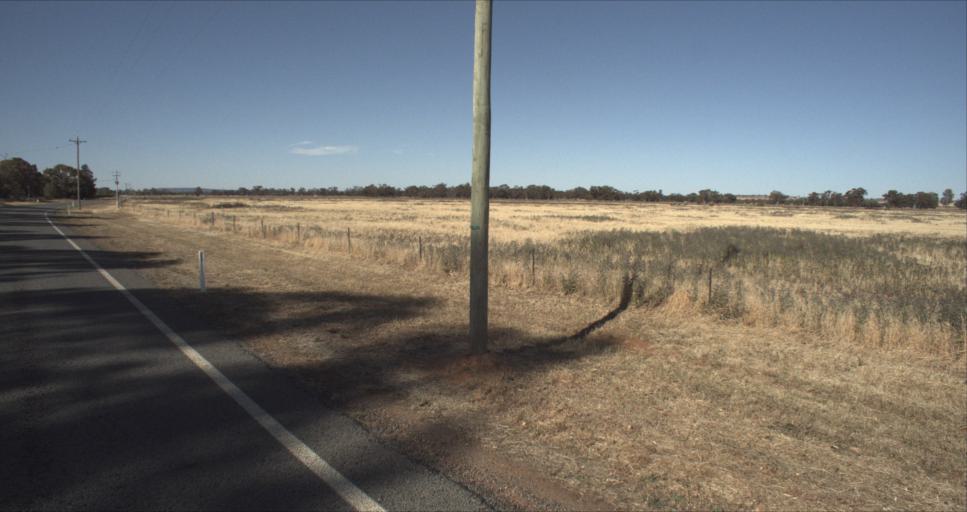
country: AU
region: New South Wales
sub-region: Leeton
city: Leeton
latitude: -34.6233
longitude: 146.3955
